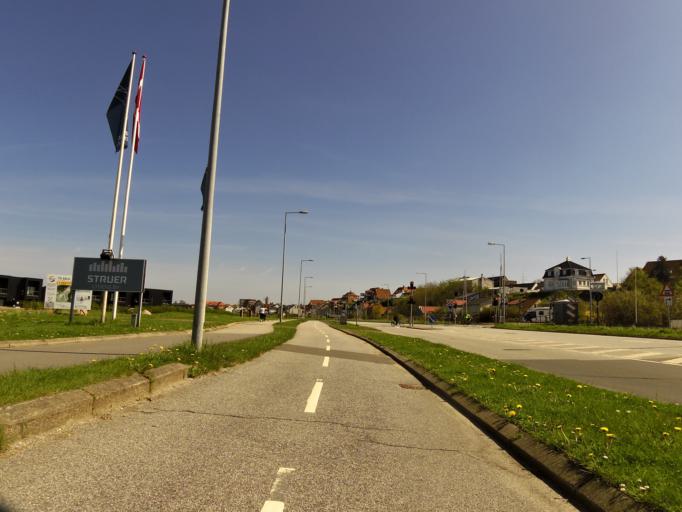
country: DK
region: Central Jutland
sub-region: Struer Kommune
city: Struer
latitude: 56.4944
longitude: 8.5853
